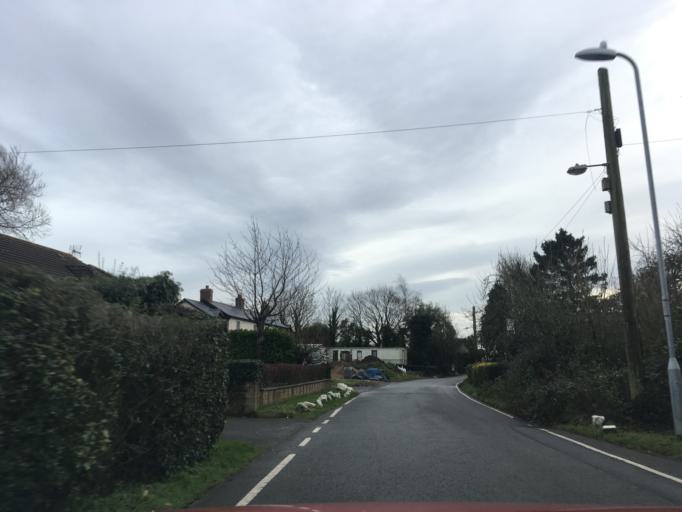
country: GB
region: Wales
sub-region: Monmouthshire
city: Magor
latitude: 51.5745
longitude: -2.8237
